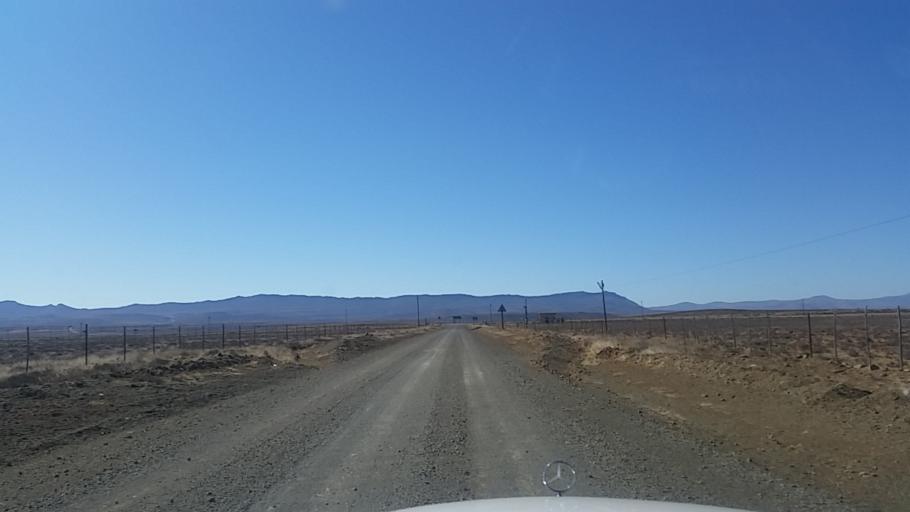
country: ZA
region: Eastern Cape
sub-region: Cacadu District Municipality
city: Graaff-Reinet
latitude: -31.9088
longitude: 24.7619
